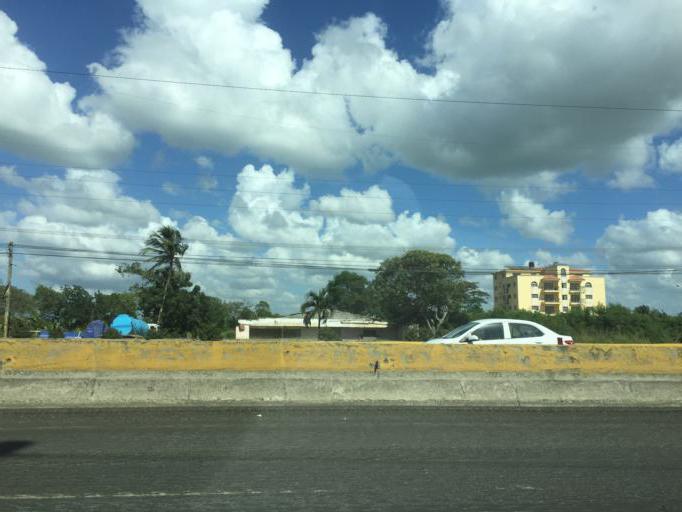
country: DO
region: Santo Domingo
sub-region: Santo Domingo
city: Boca Chica
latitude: 18.4552
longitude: -69.7006
